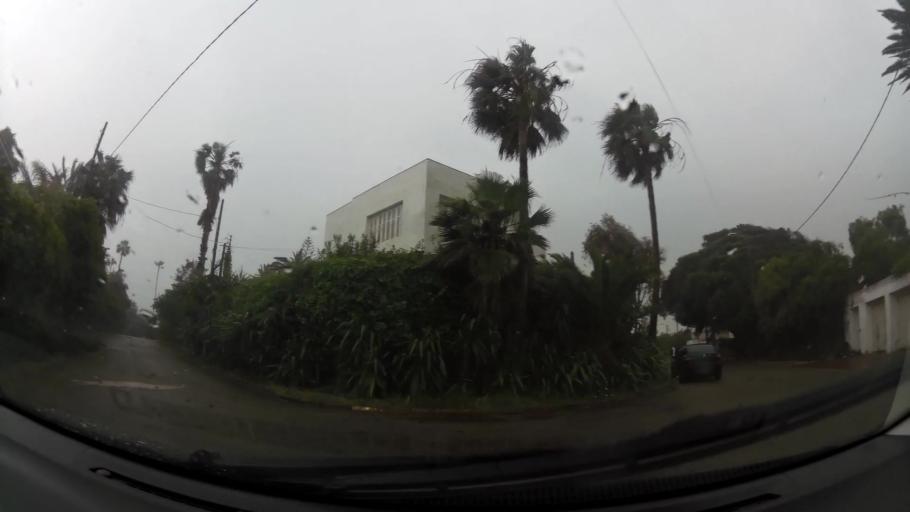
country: MA
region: Grand Casablanca
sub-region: Casablanca
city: Casablanca
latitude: 33.5879
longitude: -7.6798
